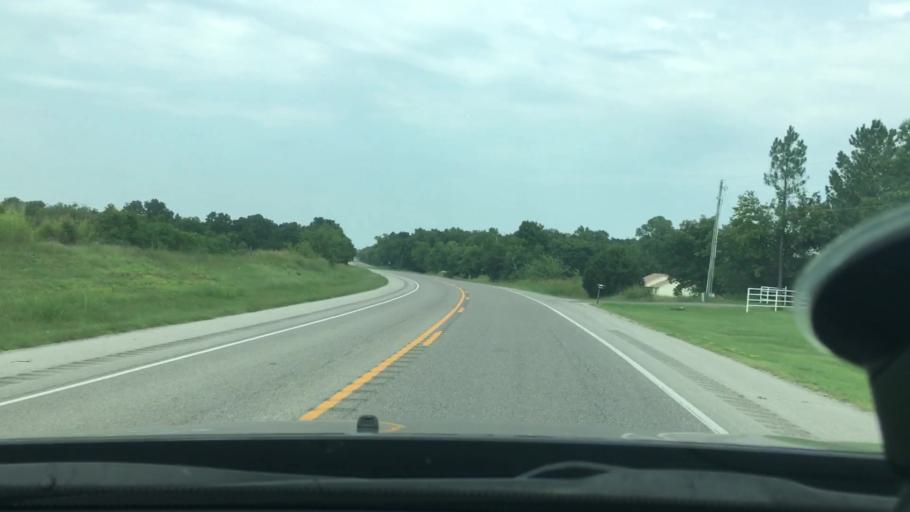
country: US
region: Oklahoma
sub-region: Murray County
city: Sulphur
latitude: 34.5312
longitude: -96.9675
